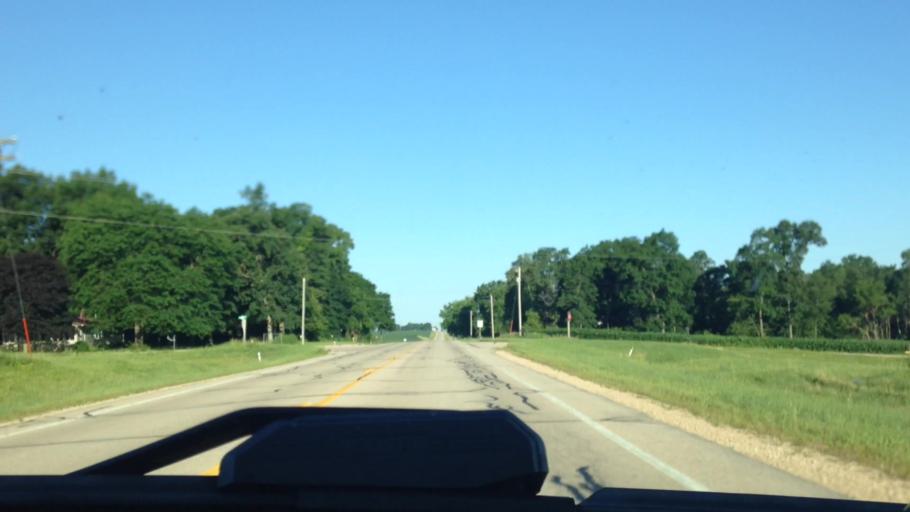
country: US
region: Wisconsin
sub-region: Dane County
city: De Forest
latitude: 43.3321
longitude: -89.3041
